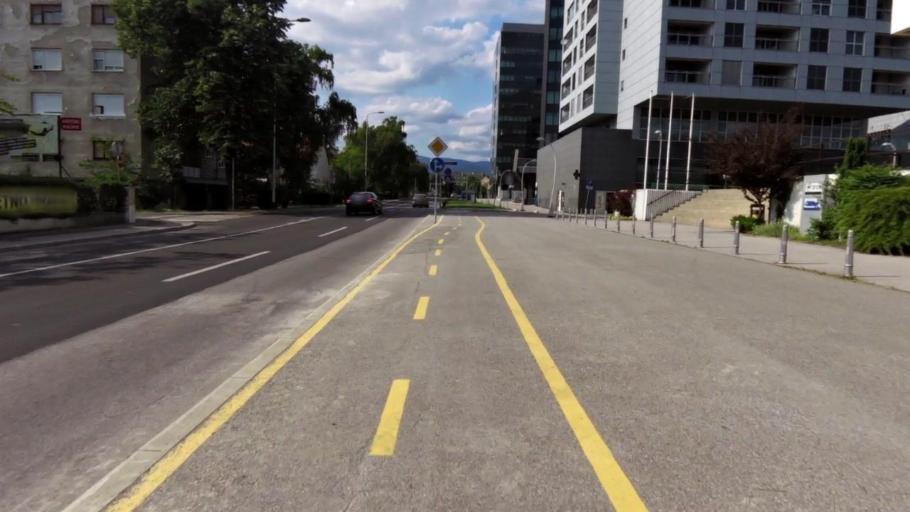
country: HR
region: Grad Zagreb
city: Novi Zagreb
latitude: 45.7923
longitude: 15.9692
